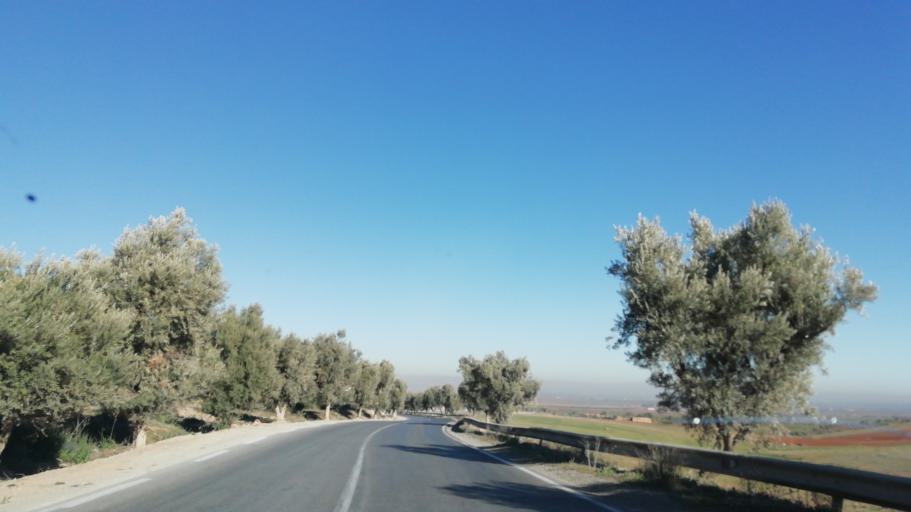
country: DZ
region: Mascara
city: Mascara
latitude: 35.2486
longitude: 0.1213
